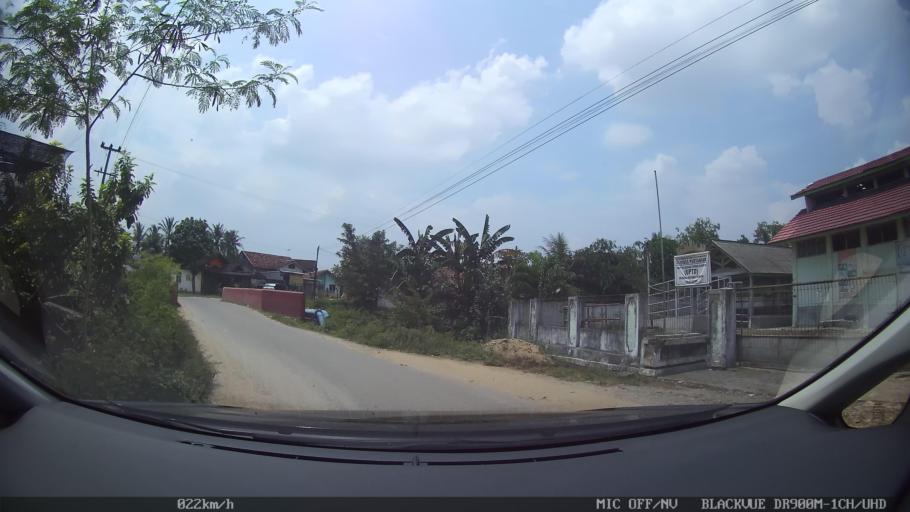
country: ID
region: Lampung
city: Pringsewu
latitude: -5.3454
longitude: 104.9859
